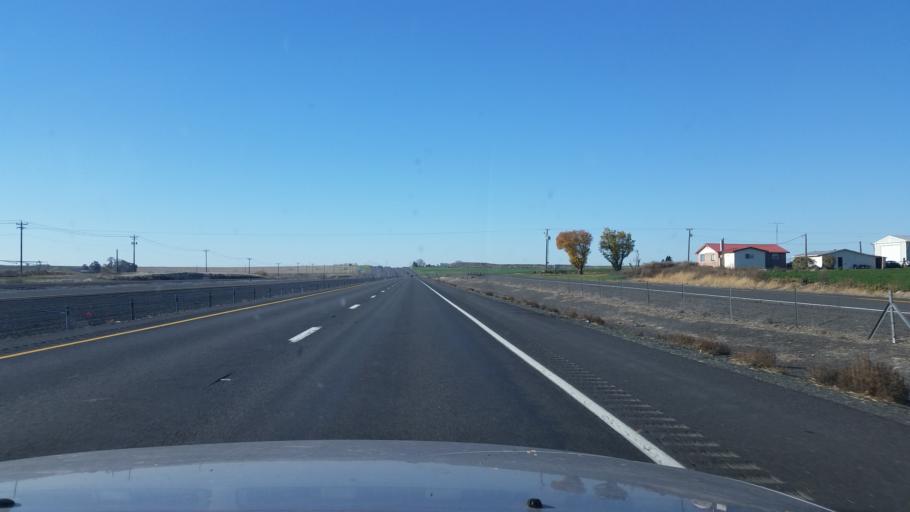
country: US
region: Washington
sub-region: Grant County
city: Warden
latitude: 47.0862
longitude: -119.0636
